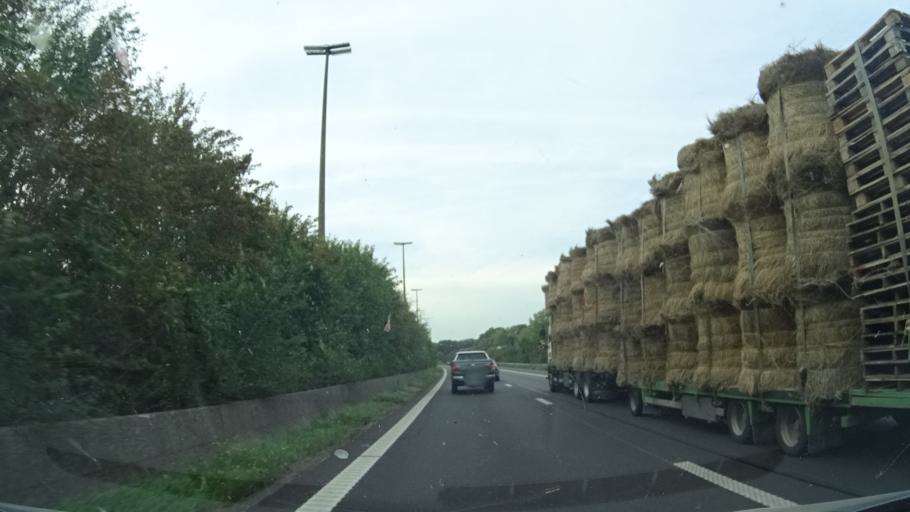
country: BE
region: Wallonia
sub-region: Province du Hainaut
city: Bernissart
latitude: 50.5026
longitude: 3.6799
